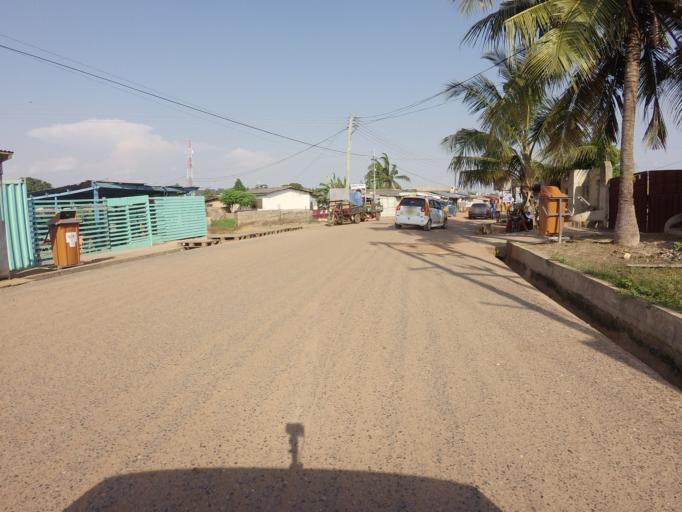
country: GH
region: Greater Accra
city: Dome
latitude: 5.6137
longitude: -0.2365
